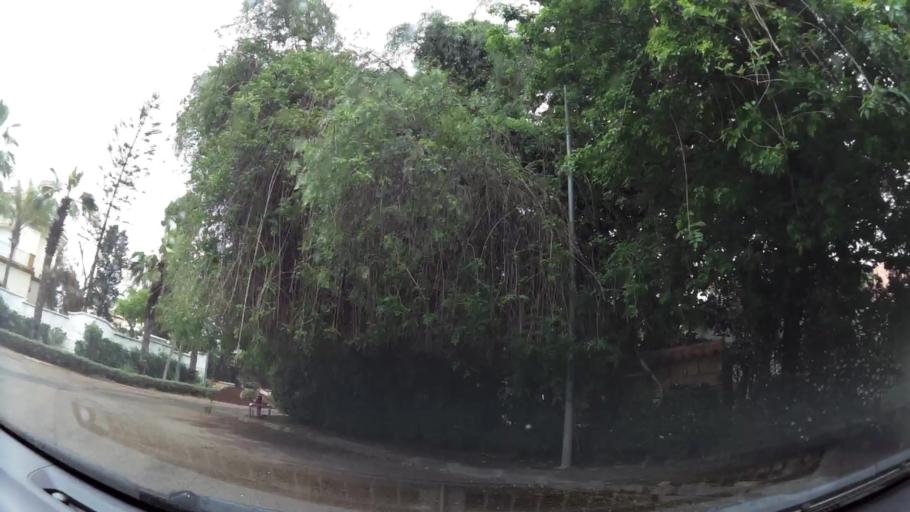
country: MA
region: Grand Casablanca
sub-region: Casablanca
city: Casablanca
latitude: 33.5336
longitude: -7.6266
